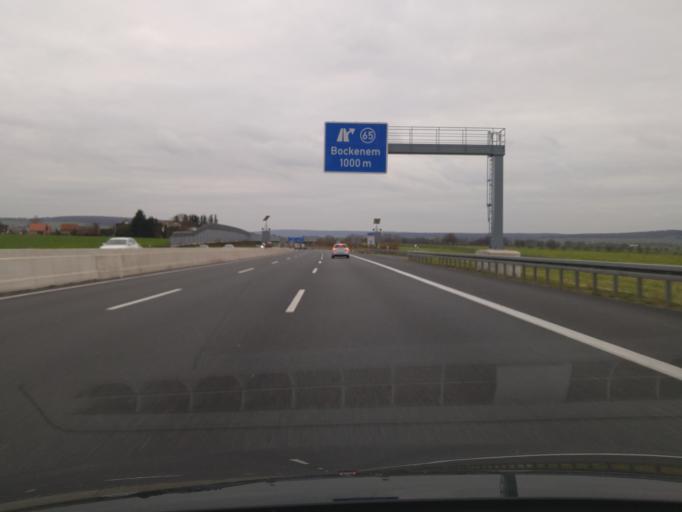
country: DE
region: Lower Saxony
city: Bockenem
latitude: 52.0095
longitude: 10.1611
